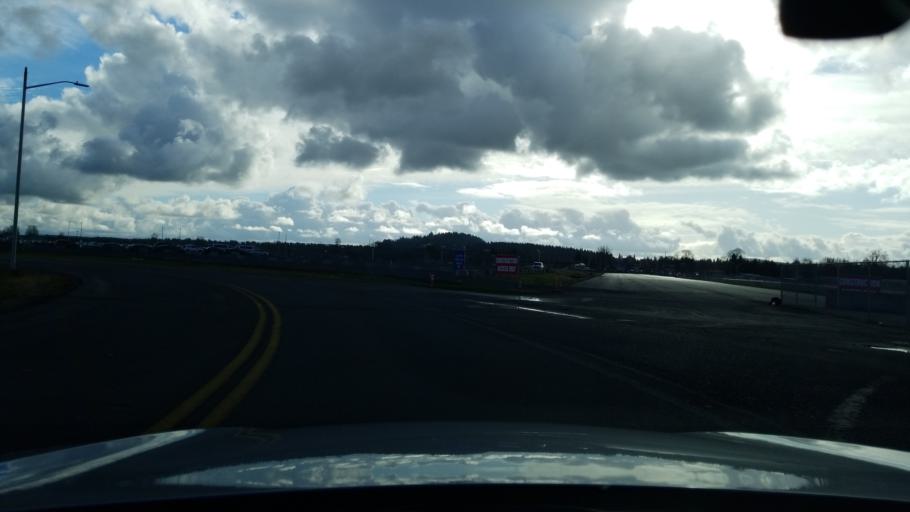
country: US
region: Washington
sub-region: Clark County
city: Orchards
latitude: 45.5806
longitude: -122.5776
